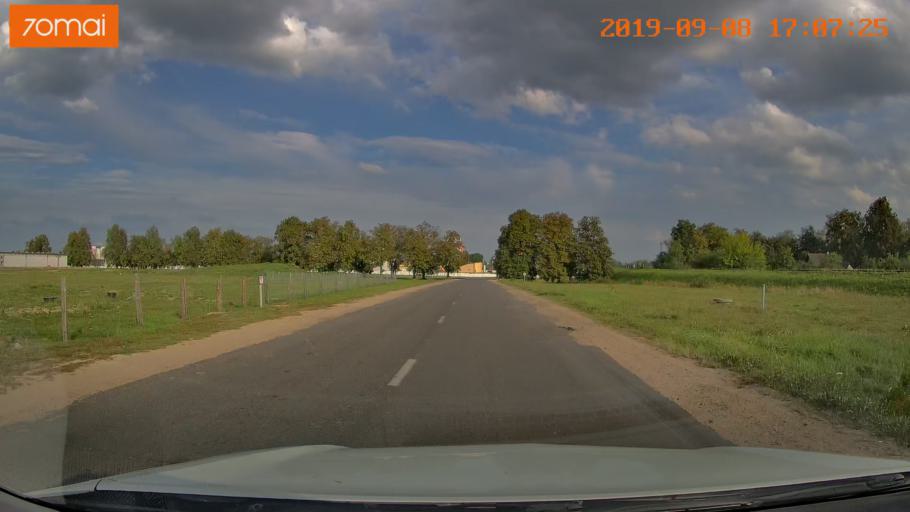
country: BY
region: Grodnenskaya
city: Hrodna
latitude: 53.6651
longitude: 23.9618
